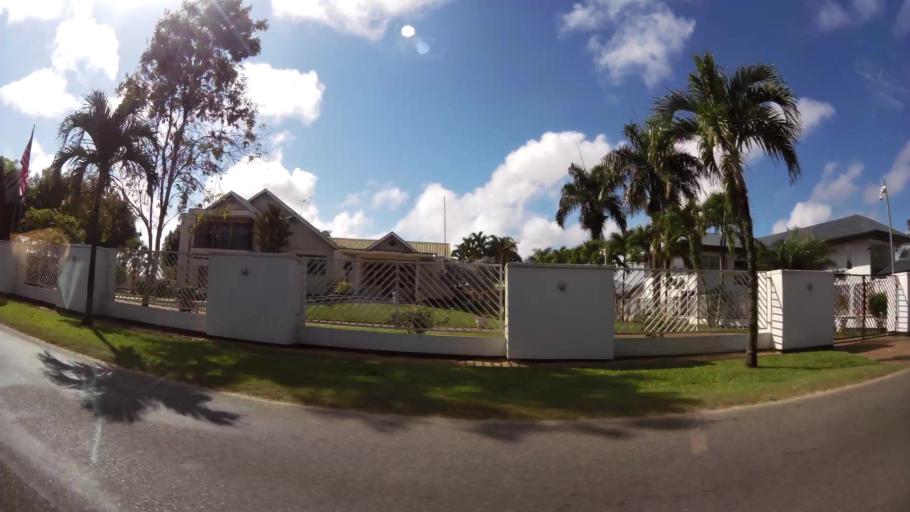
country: SR
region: Commewijne
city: Nieuw Amsterdam
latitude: 5.8452
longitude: -55.1134
